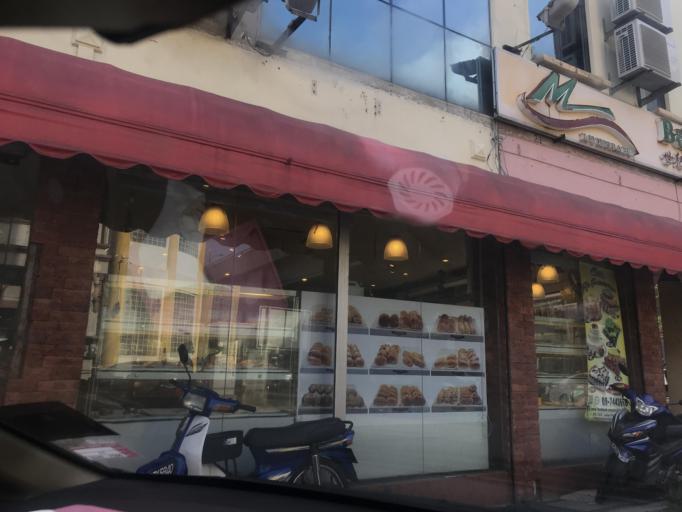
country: MY
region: Kelantan
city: Kota Bharu
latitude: 6.1163
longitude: 102.2402
